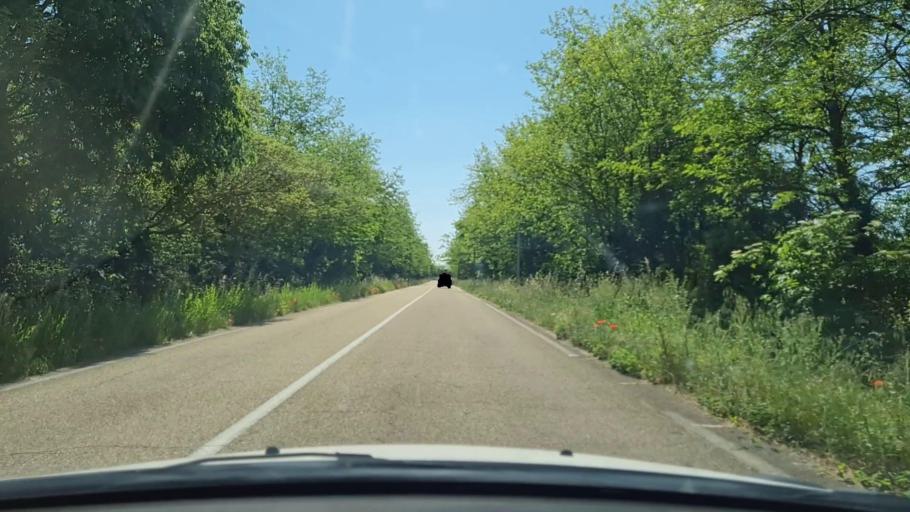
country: FR
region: Languedoc-Roussillon
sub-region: Departement du Gard
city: Vezenobres
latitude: 44.0199
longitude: 4.1520
